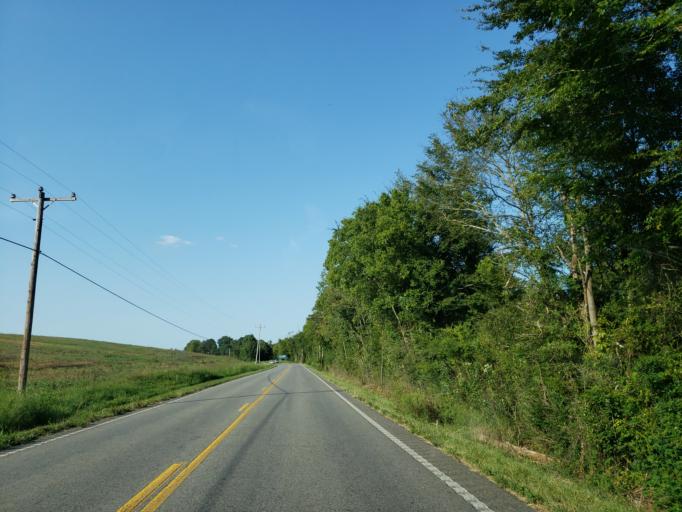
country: US
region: Tennessee
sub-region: Bradley County
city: Wildwood Lake
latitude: 34.9944
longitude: -84.7365
